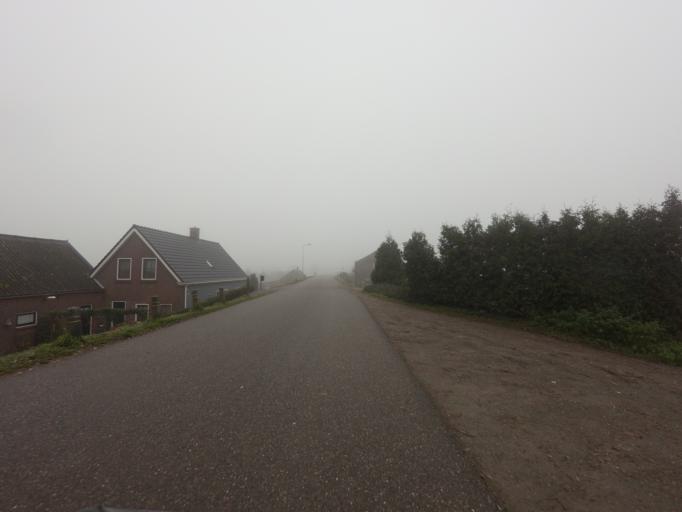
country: NL
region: Gelderland
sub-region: Gemeente Zaltbommel
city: Nederhemert
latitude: 51.7647
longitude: 5.1507
